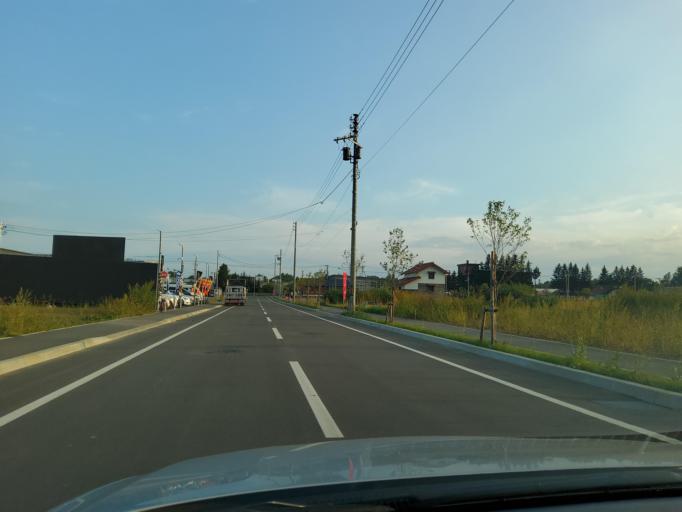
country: JP
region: Hokkaido
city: Obihiro
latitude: 42.9353
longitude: 143.1534
